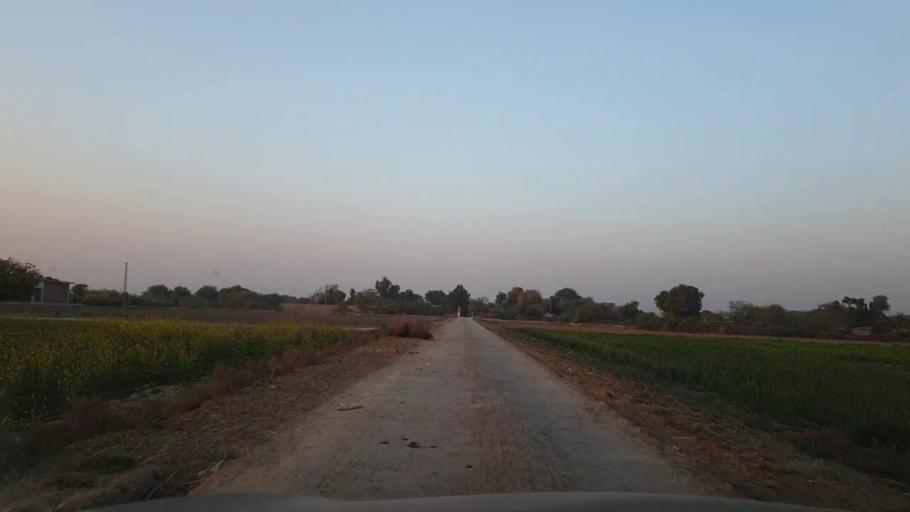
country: PK
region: Sindh
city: Mirpur Khas
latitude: 25.5967
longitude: 68.8523
